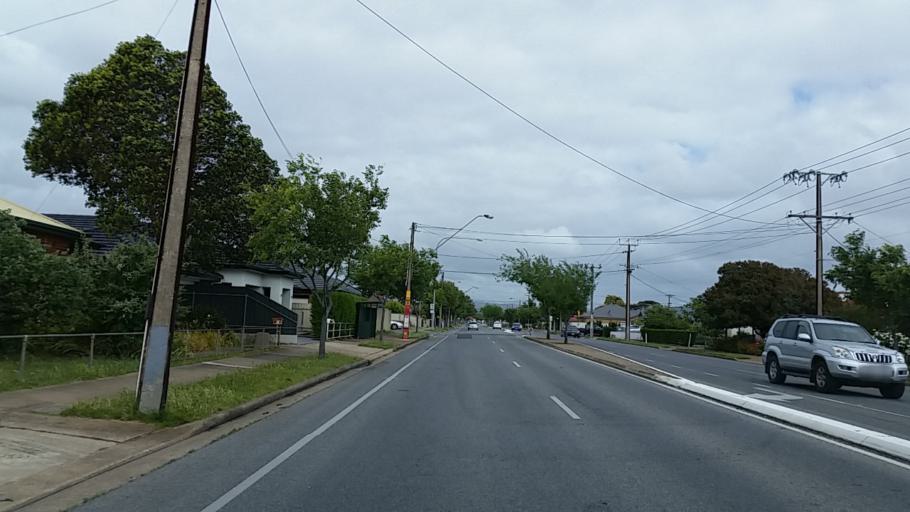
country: AU
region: South Australia
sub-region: Charles Sturt
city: Findon
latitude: -34.9002
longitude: 138.5395
